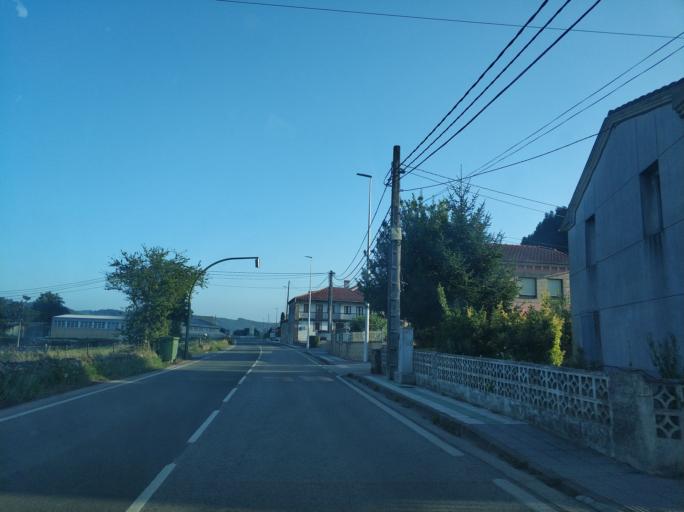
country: ES
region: Cantabria
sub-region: Provincia de Cantabria
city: Puente Viesgo
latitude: 43.3593
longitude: -3.9559
